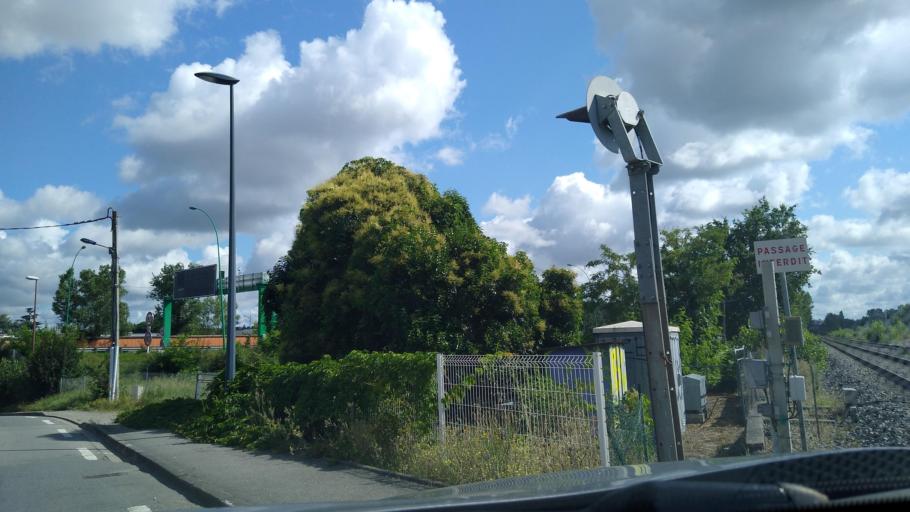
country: FR
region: Midi-Pyrenees
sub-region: Departement de la Haute-Garonne
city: L'Union
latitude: 43.6371
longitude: 1.4823
